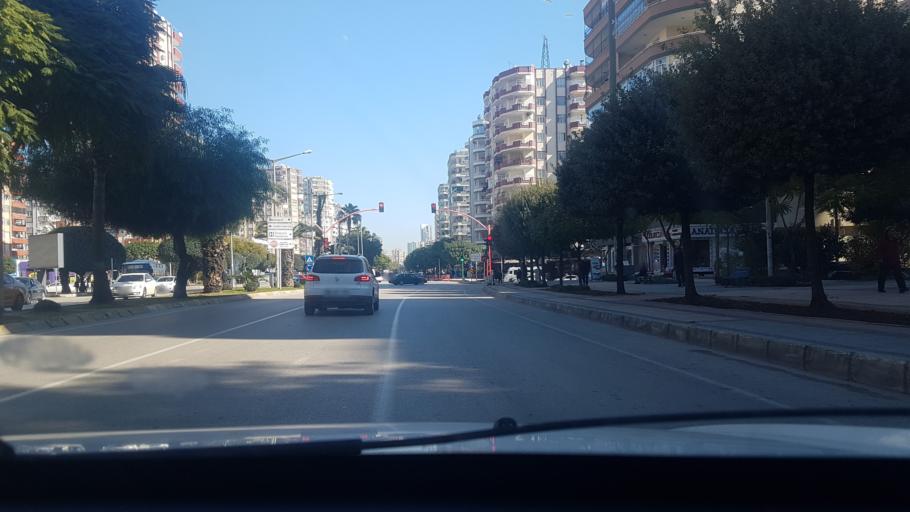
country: TR
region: Adana
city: Adana
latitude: 37.0484
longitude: 35.2855
